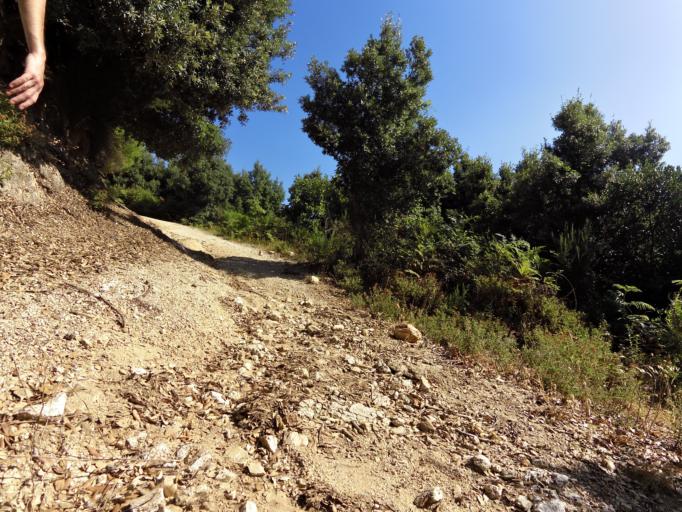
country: IT
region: Calabria
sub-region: Provincia di Reggio Calabria
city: Bivongi
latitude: 38.5035
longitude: 16.4404
